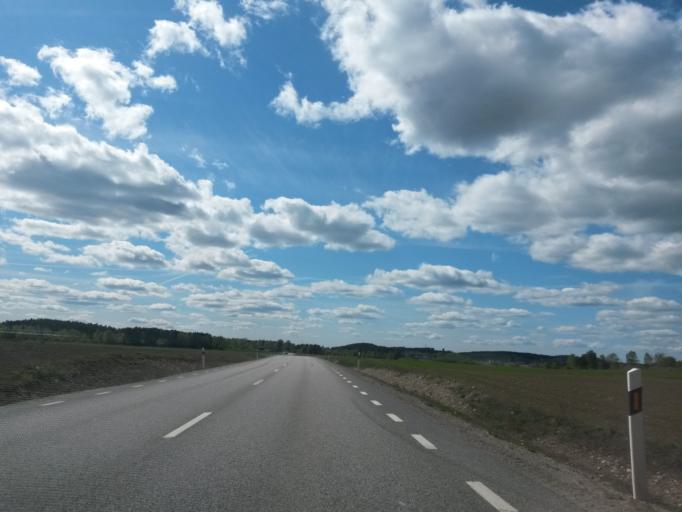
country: SE
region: Vaestra Goetaland
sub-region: Vargarda Kommun
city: Vargarda
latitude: 58.0493
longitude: 12.8446
